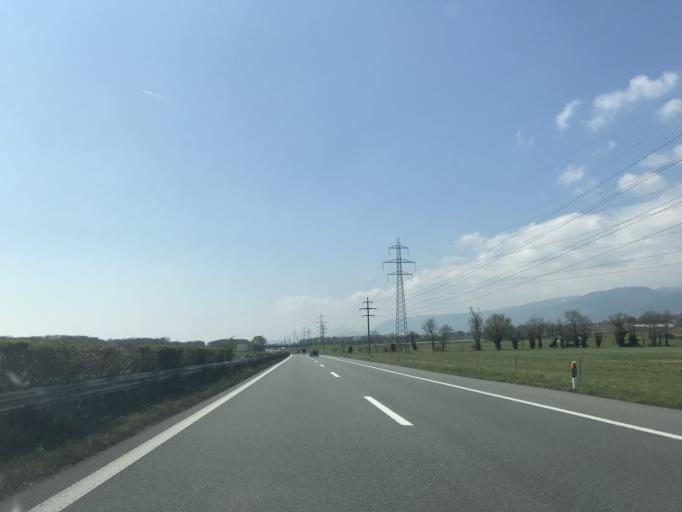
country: CH
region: Vaud
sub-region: Nyon District
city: Gland
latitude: 46.4392
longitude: 6.2823
